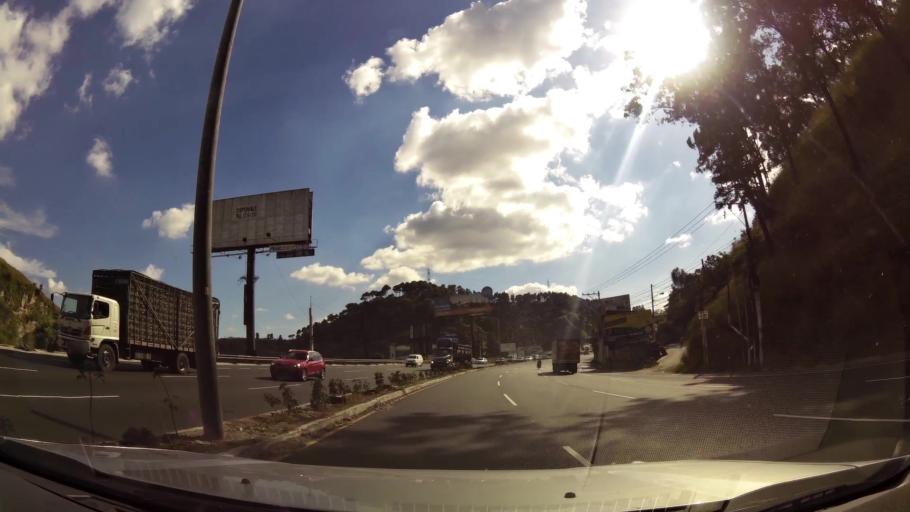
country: GT
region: Guatemala
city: Villa Nueva
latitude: 14.5497
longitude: -90.5785
